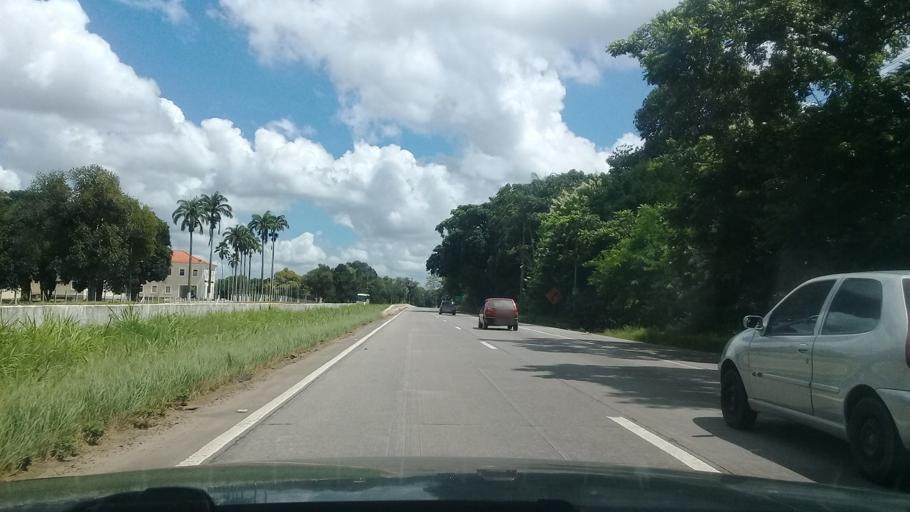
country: BR
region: Pernambuco
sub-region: Carpina
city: Carpina
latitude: -7.9247
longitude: -35.1528
